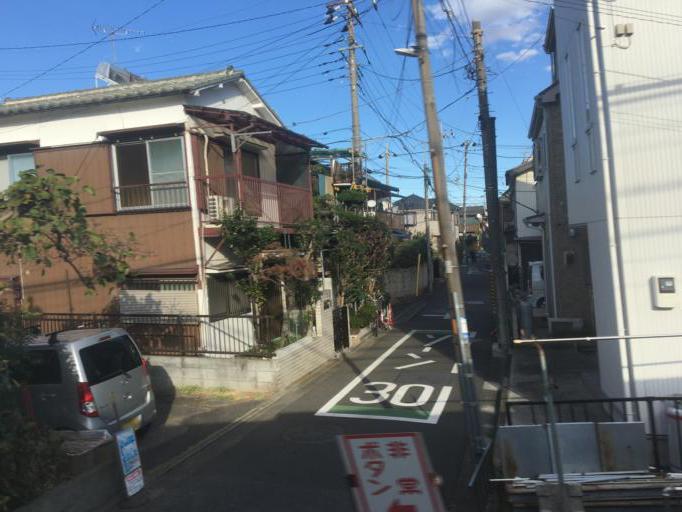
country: JP
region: Saitama
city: Oi
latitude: 35.8507
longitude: 139.5324
